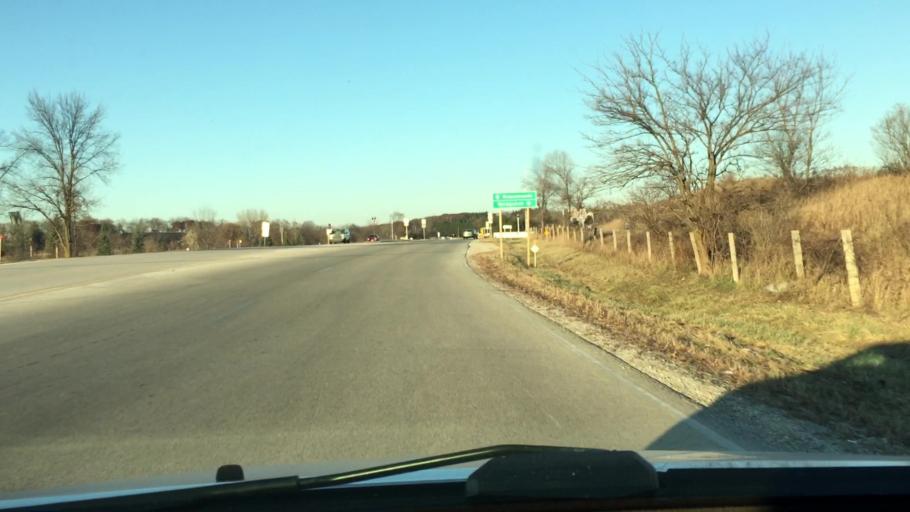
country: US
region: Wisconsin
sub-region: Waukesha County
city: Pewaukee
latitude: 43.0930
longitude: -88.2741
